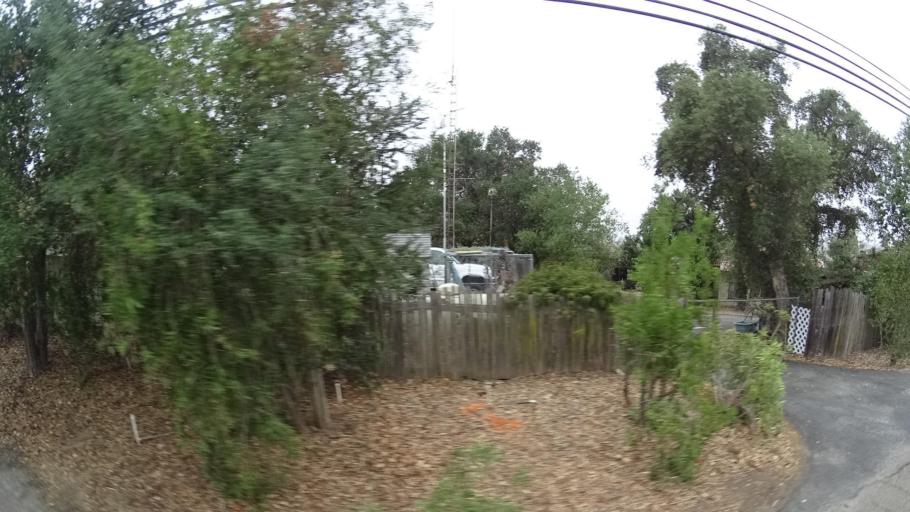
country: US
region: California
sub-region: San Diego County
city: Fallbrook
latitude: 33.3875
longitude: -117.2159
